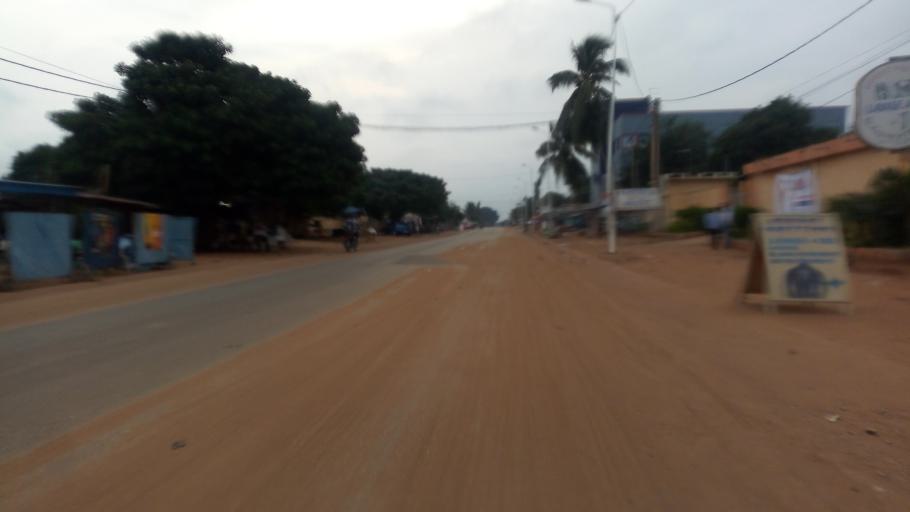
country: TG
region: Maritime
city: Lome
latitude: 6.1810
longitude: 1.1922
